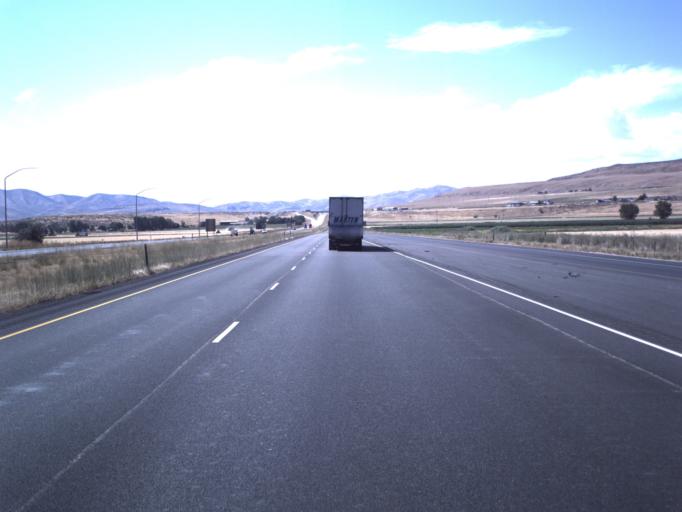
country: US
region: Utah
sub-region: Box Elder County
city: Tremonton
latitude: 41.7118
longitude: -112.2077
